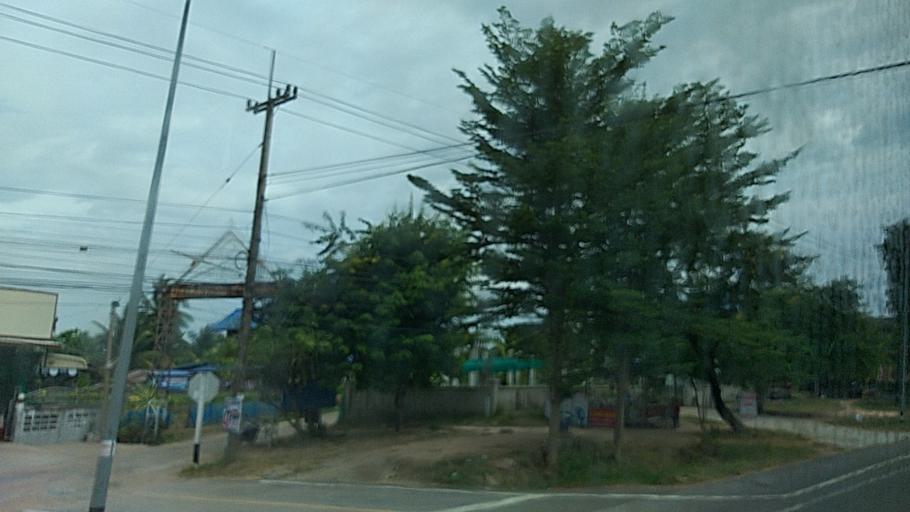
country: TH
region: Maha Sarakham
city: Maha Sarakham
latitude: 16.1568
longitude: 103.3690
